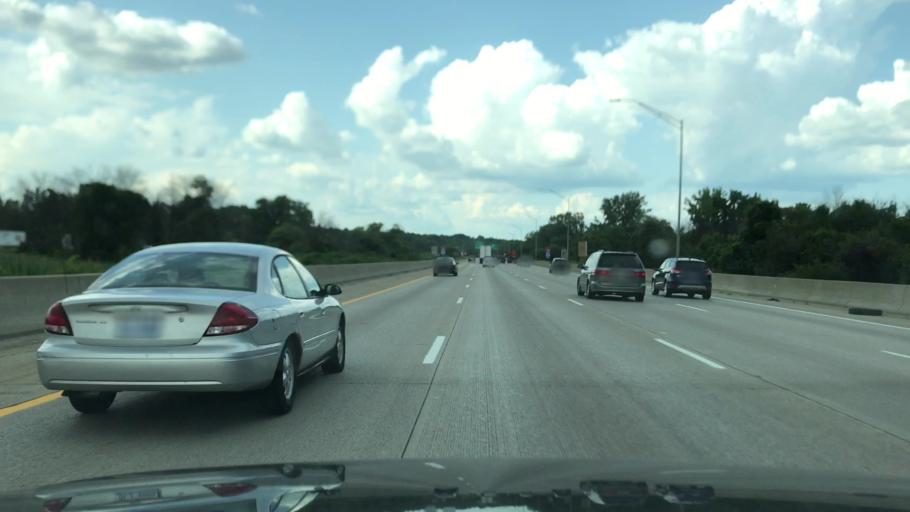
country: US
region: Michigan
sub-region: Kent County
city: Comstock Park
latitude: 43.0054
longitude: -85.6752
